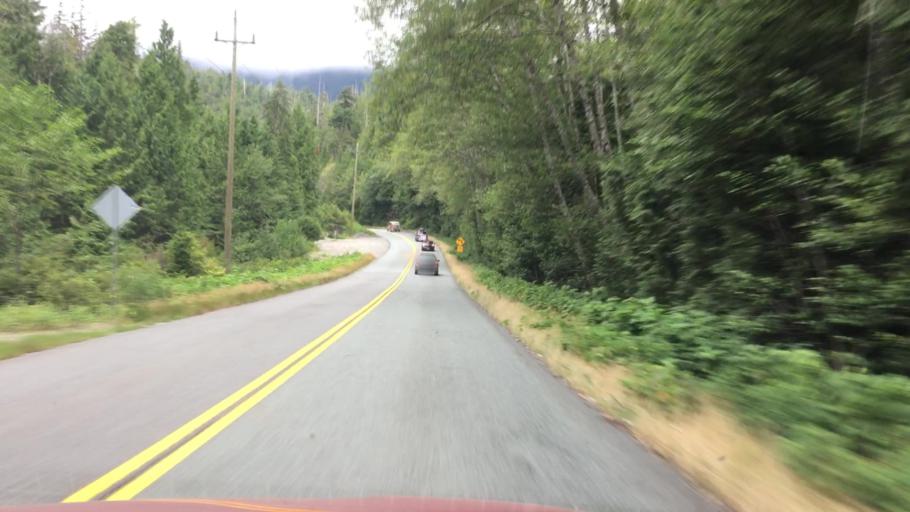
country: CA
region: British Columbia
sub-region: Regional District of Alberni-Clayoquot
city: Ucluelet
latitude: 49.1021
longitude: -125.4530
